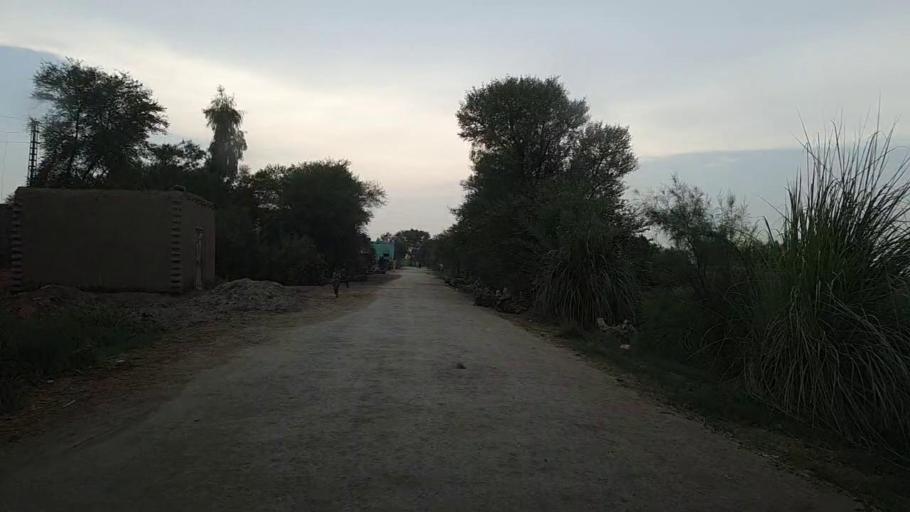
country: PK
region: Sindh
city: Khanpur
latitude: 27.8389
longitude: 69.4818
